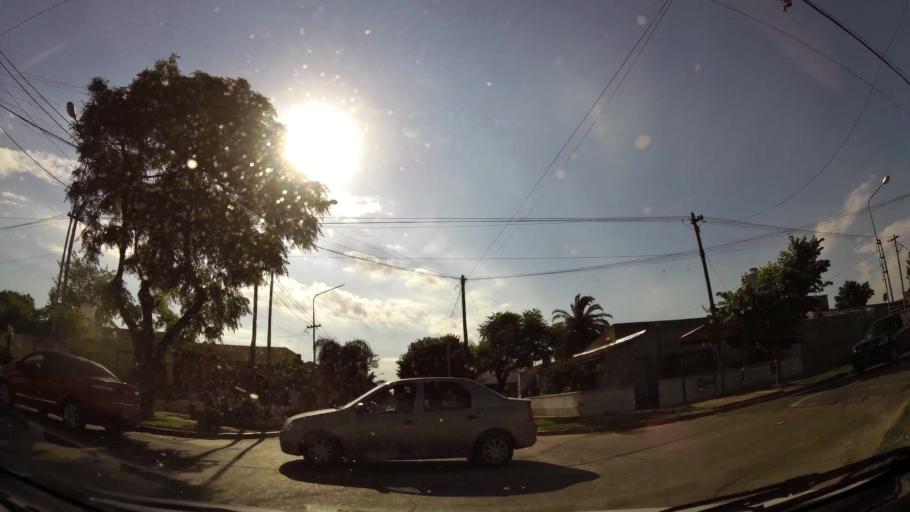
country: AR
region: Buenos Aires
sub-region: Partido de Merlo
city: Merlo
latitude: -34.6575
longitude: -58.7186
